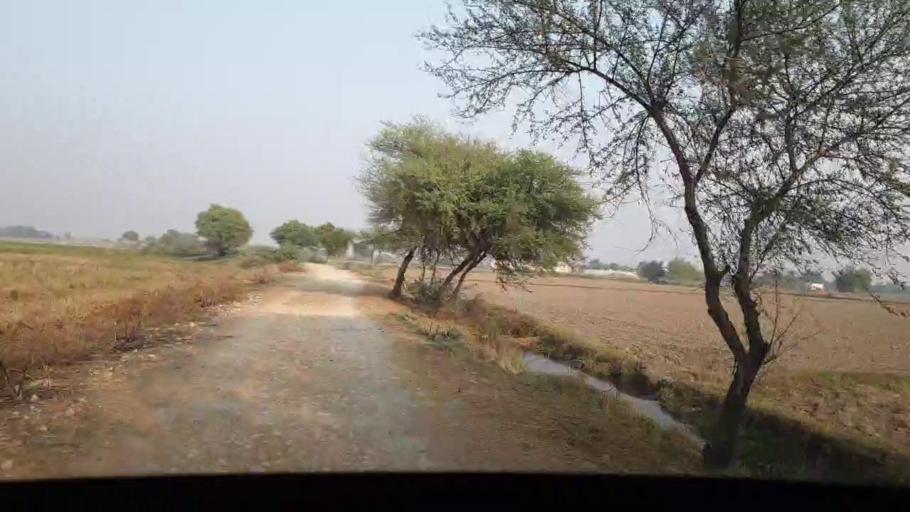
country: PK
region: Sindh
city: Chuhar Jamali
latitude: 24.2558
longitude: 68.1099
